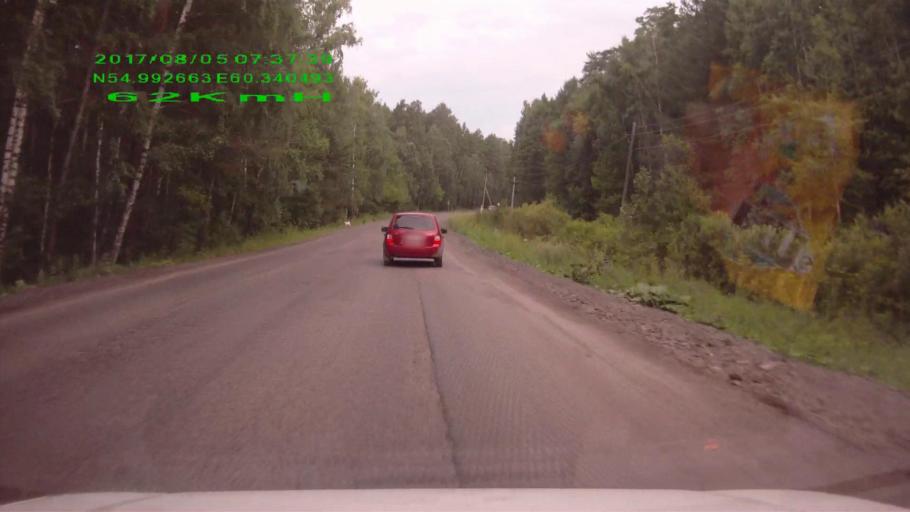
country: RU
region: Chelyabinsk
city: Chebarkul'
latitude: 54.9929
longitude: 60.3401
